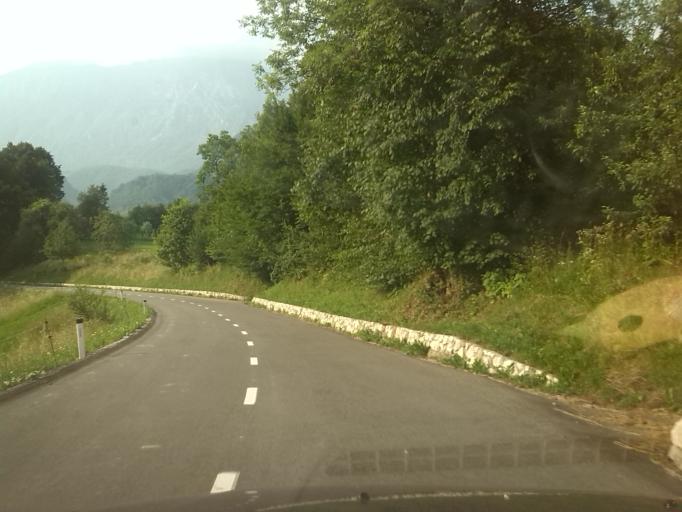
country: SI
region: Kobarid
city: Kobarid
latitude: 46.2281
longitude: 13.5920
